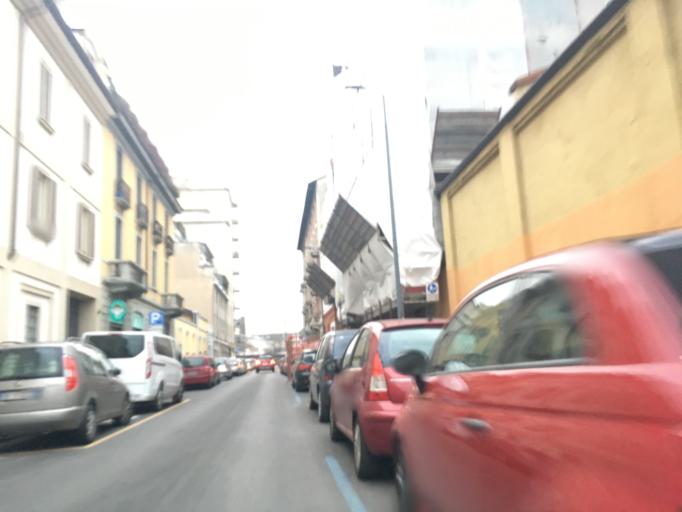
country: IT
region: Lombardy
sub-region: Citta metropolitana di Milano
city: Milano
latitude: 45.4484
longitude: 9.1647
